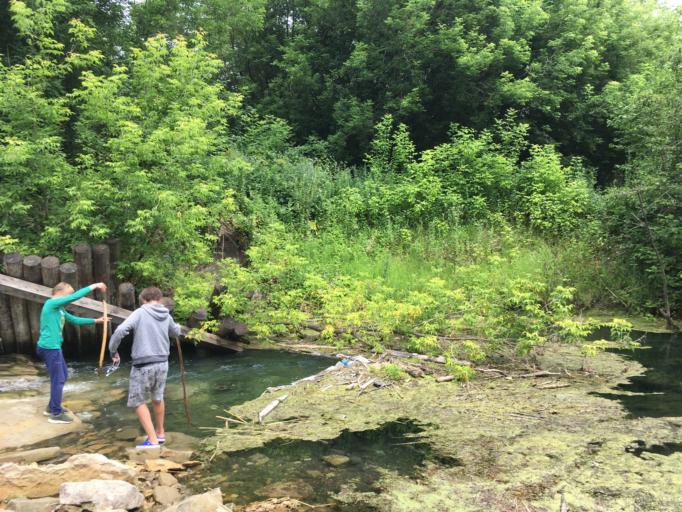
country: RU
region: Tatarstan
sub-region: Gorod Kazan'
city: Kazan
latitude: 55.9015
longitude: 49.1565
